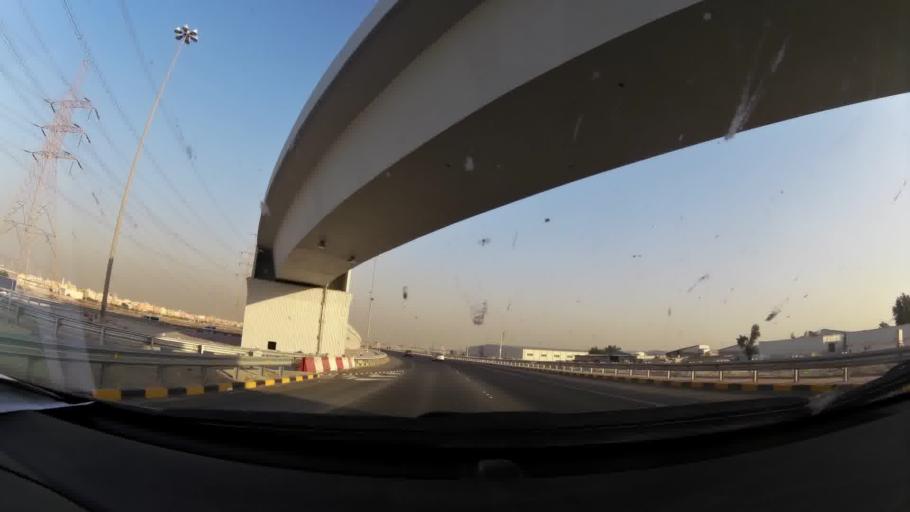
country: KW
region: Muhafazat al Jahra'
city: Al Jahra'
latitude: 29.2960
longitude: 47.7887
